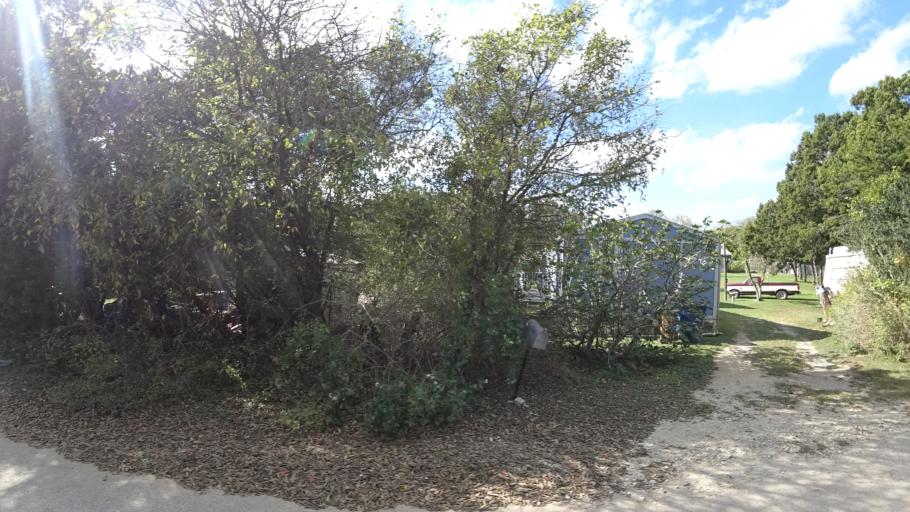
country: US
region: Texas
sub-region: Travis County
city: Barton Creek
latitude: 30.2471
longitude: -97.8807
